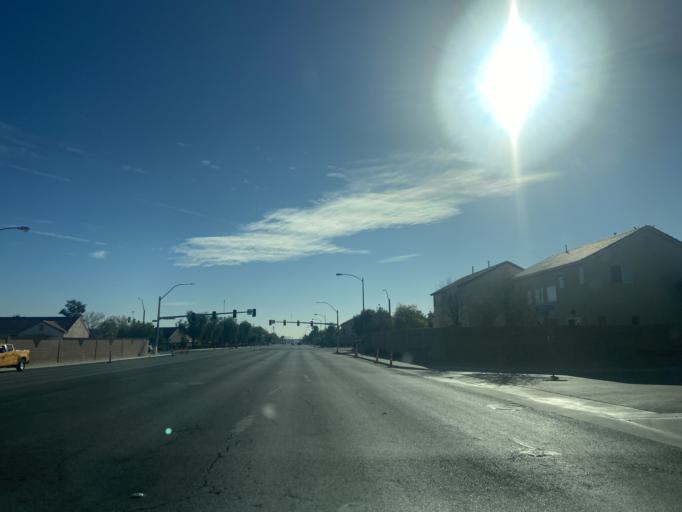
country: US
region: Nevada
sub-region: Clark County
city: North Las Vegas
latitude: 36.2701
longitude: -115.1799
